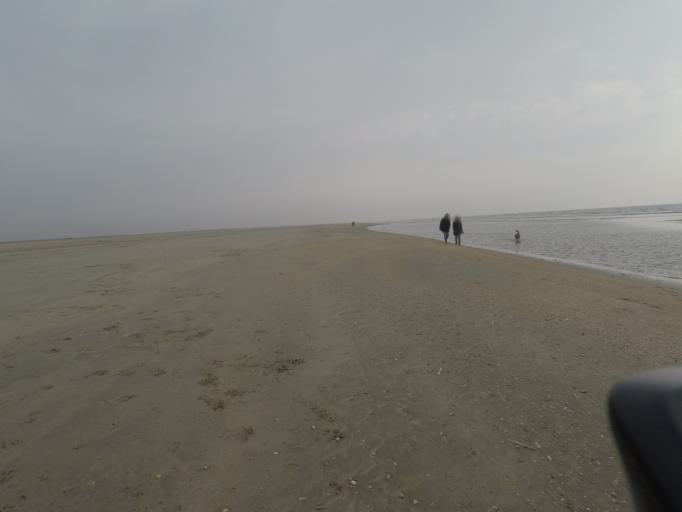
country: DE
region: Schleswig-Holstein
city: List
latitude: 55.1624
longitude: 8.4765
